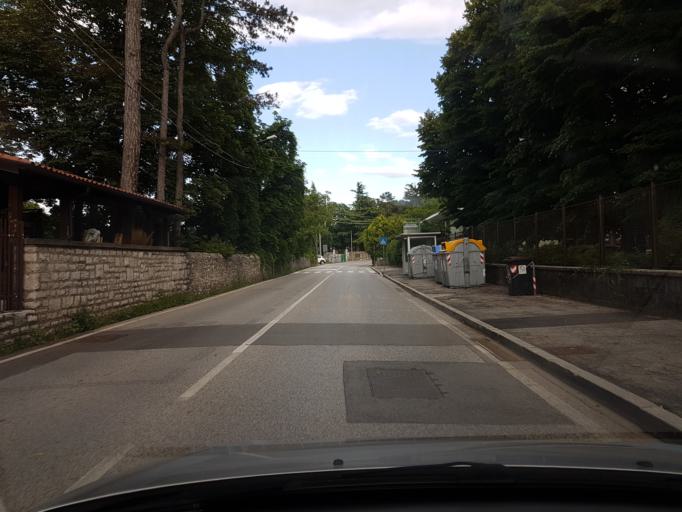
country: IT
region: Friuli Venezia Giulia
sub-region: Provincia di Trieste
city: Villa Opicina
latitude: 45.6882
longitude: 13.7914
